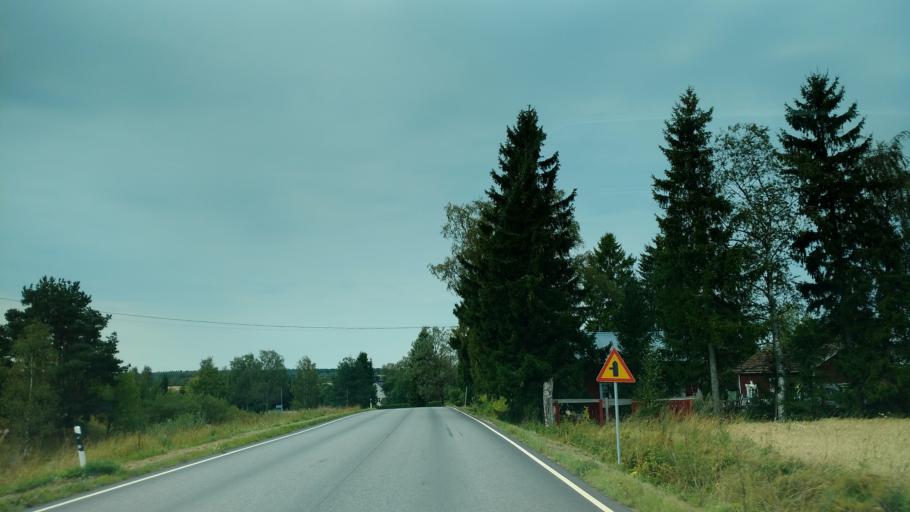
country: FI
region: Varsinais-Suomi
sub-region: Loimaa
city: Koski Tl
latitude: 60.6424
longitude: 23.1101
